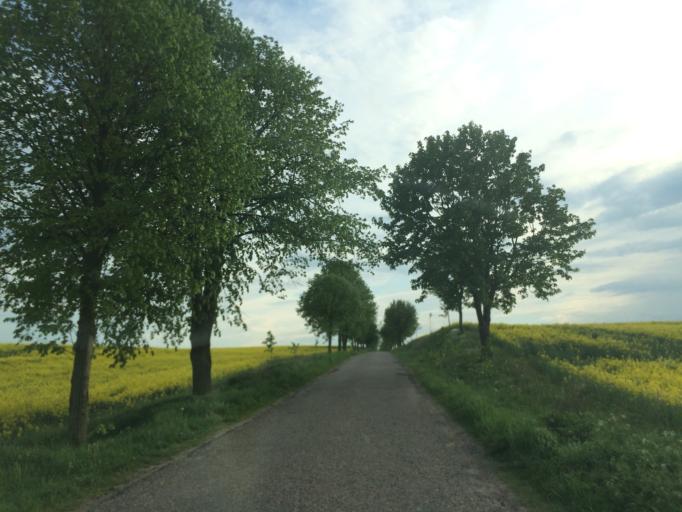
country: PL
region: Kujawsko-Pomorskie
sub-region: Powiat brodnicki
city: Brzozie
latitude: 53.3463
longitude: 19.5800
